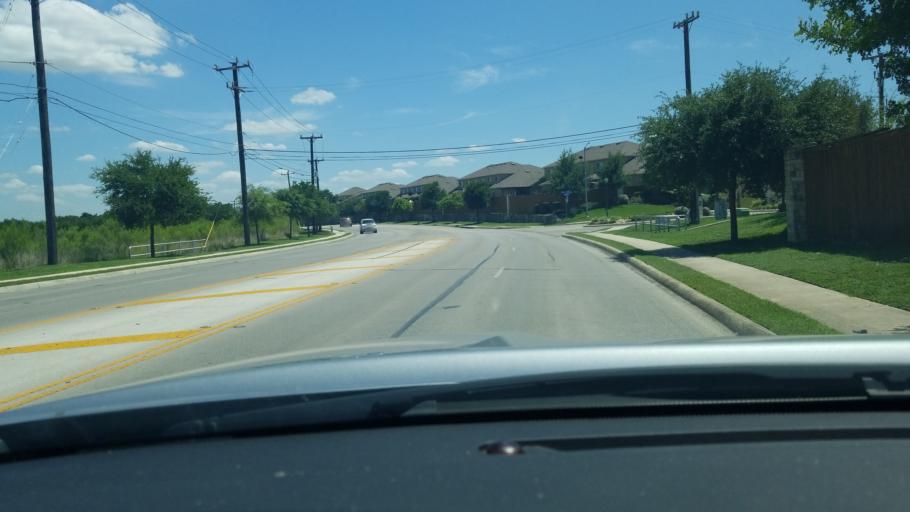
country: US
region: Texas
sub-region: Bexar County
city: Timberwood Park
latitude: 29.7006
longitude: -98.4817
